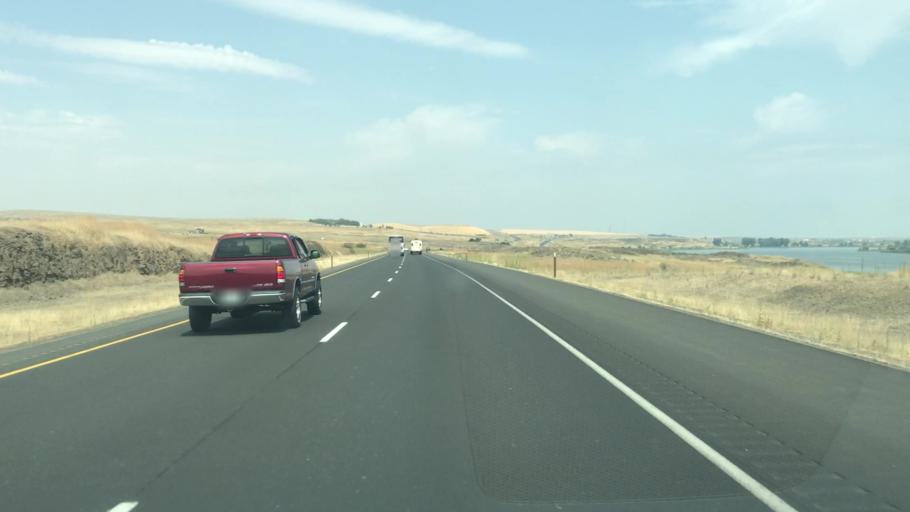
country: US
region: Washington
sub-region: Adams County
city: Ritzville
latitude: 47.2711
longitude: -118.0599
